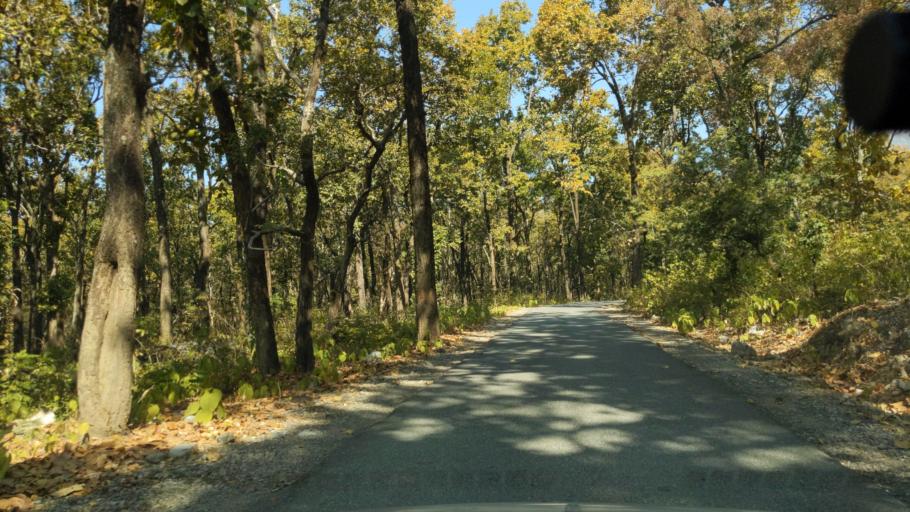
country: IN
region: Uttarakhand
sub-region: Naini Tal
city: Ramnagar
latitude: 29.4641
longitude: 79.2322
